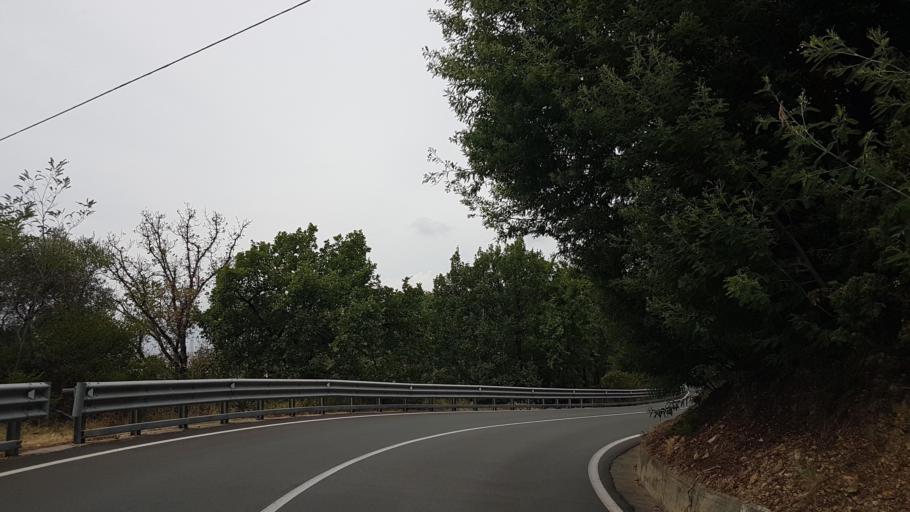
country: IT
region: Liguria
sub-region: Provincia di Genova
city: Casarza Ligure
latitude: 44.2638
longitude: 9.4412
